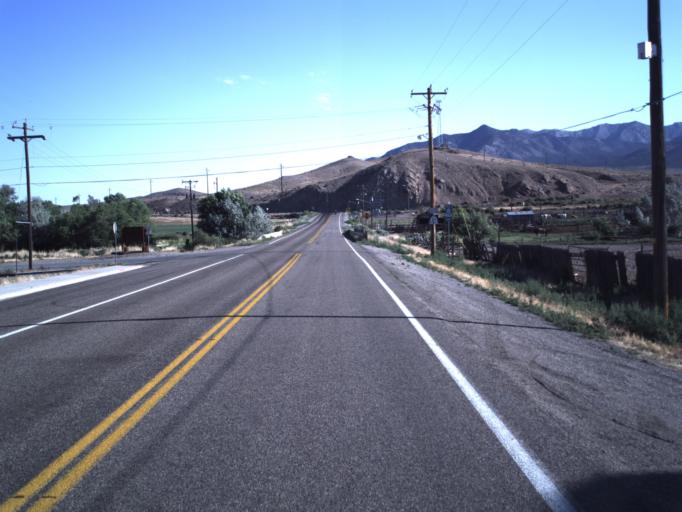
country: US
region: Utah
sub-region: Beaver County
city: Milford
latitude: 38.2163
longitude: -112.9240
